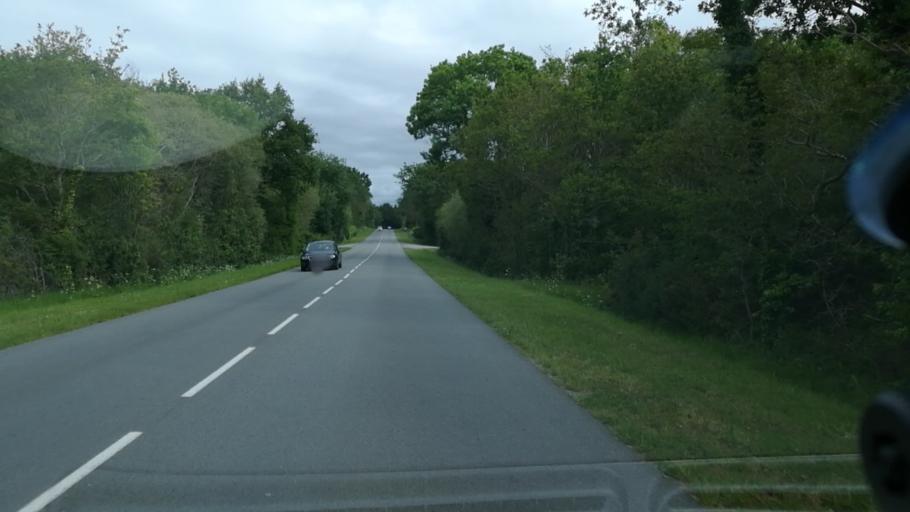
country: FR
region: Brittany
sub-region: Departement du Morbihan
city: Penestin
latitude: 47.4642
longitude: -2.4782
